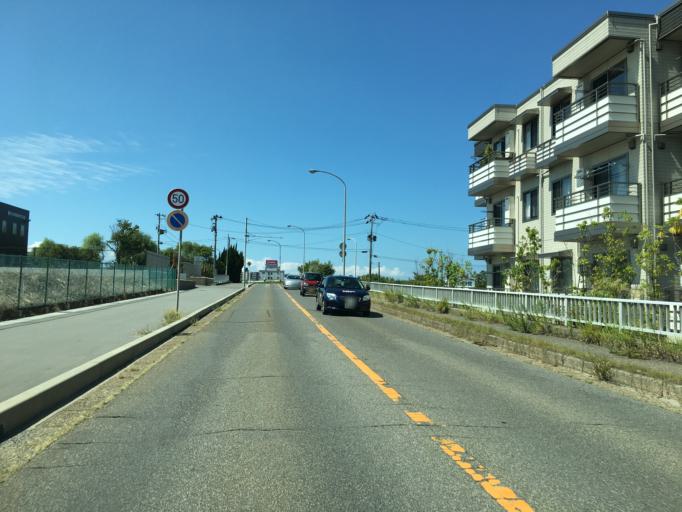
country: JP
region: Niigata
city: Niigata-shi
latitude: 37.8966
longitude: 139.0169
